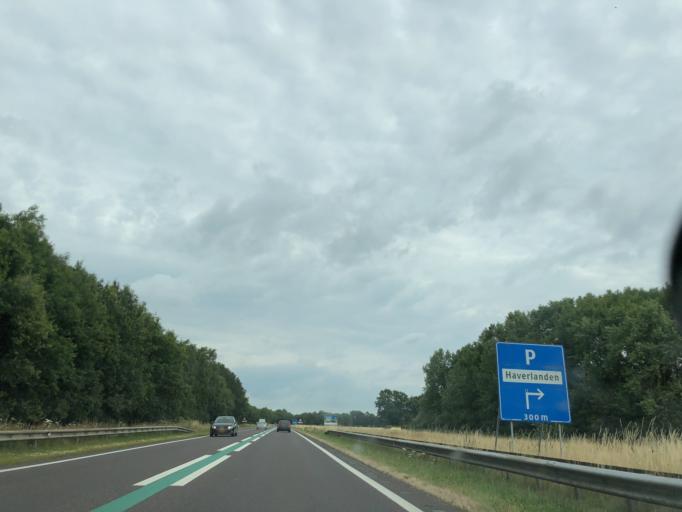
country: NL
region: Drenthe
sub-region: Gemeente Aa en Hunze
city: Anloo
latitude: 53.0293
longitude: 6.7377
